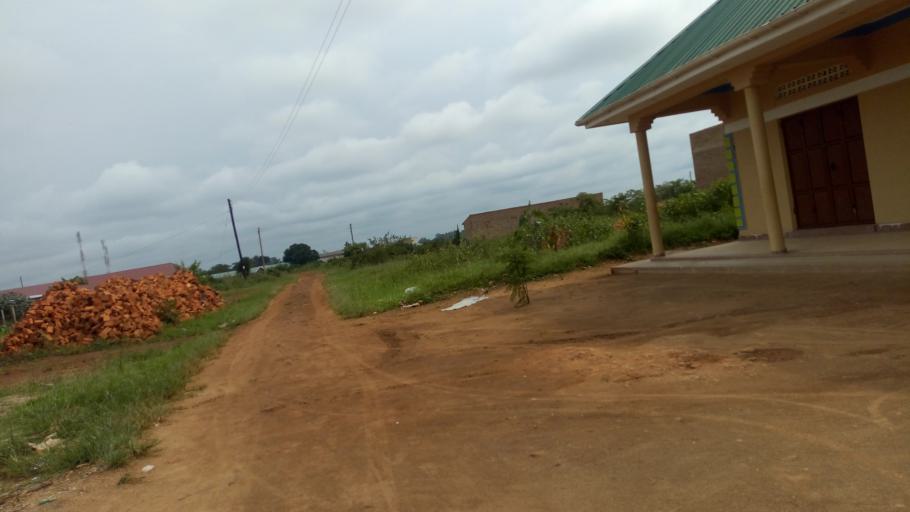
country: UG
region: Western Region
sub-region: Kiryandongo District
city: Kiryandongo
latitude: 1.8025
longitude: 32.0135
